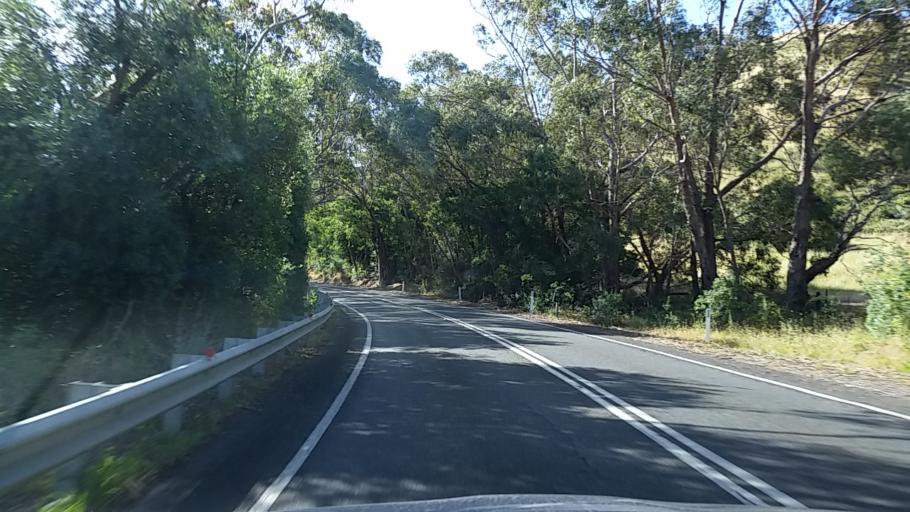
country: AU
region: South Australia
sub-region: Mount Barker
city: Meadows
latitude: -35.2717
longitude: 138.7671
